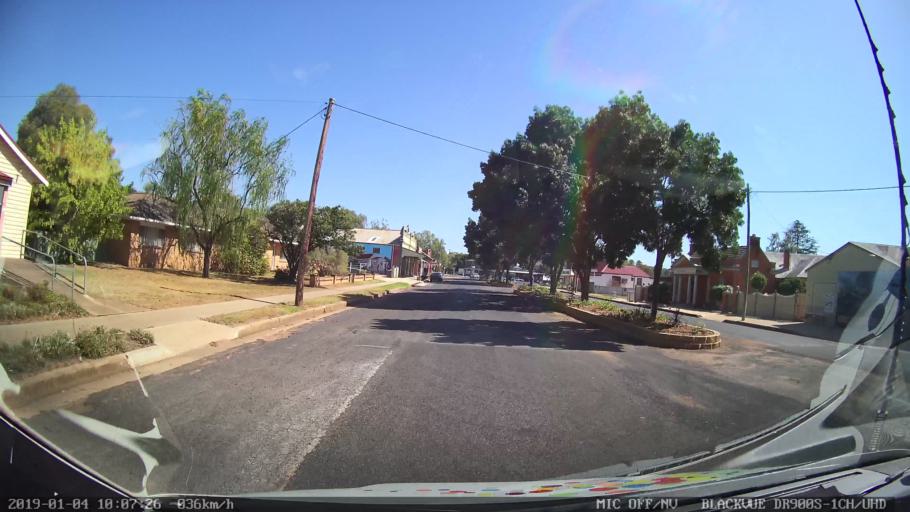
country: AU
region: New South Wales
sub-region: Cabonne
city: Canowindra
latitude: -33.4284
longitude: 148.3715
